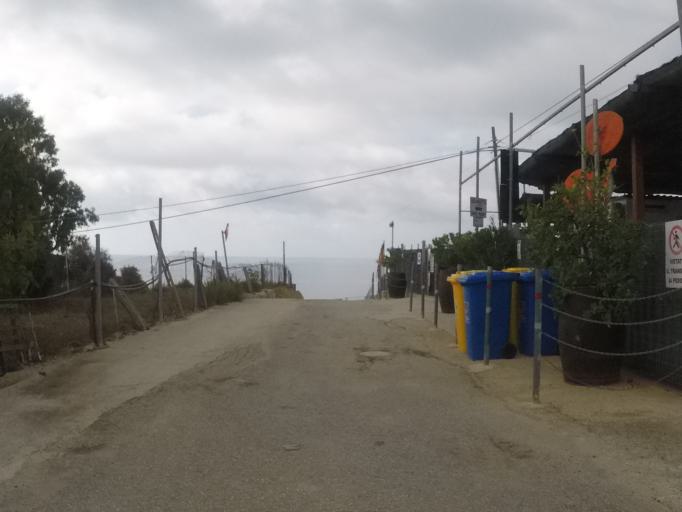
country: IT
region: Sicily
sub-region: Agrigento
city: Realmonte
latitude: 37.2897
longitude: 13.4789
